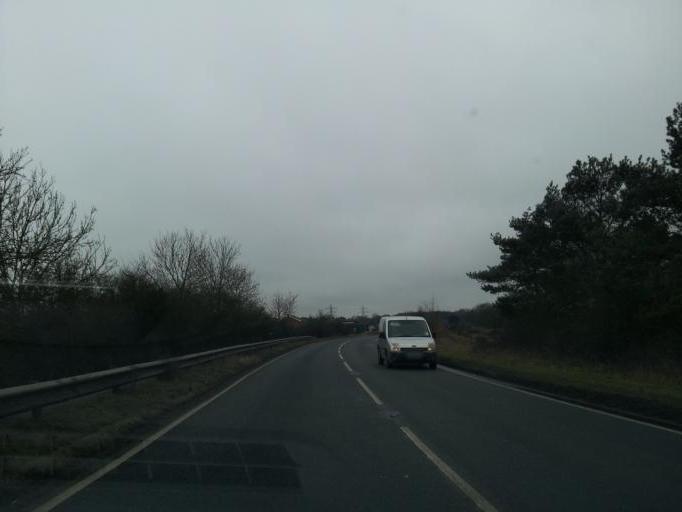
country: GB
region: England
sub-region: Essex
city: Manningtree
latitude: 51.9545
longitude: 1.0556
